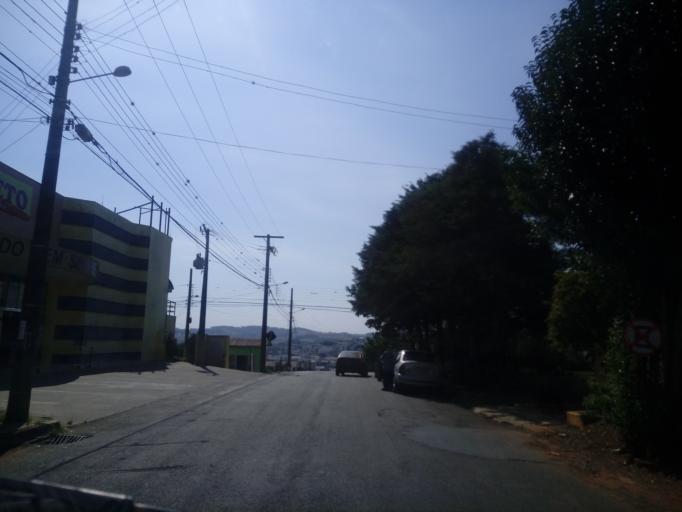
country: BR
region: Santa Catarina
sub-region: Chapeco
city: Chapeco
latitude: -27.0852
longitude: -52.6284
